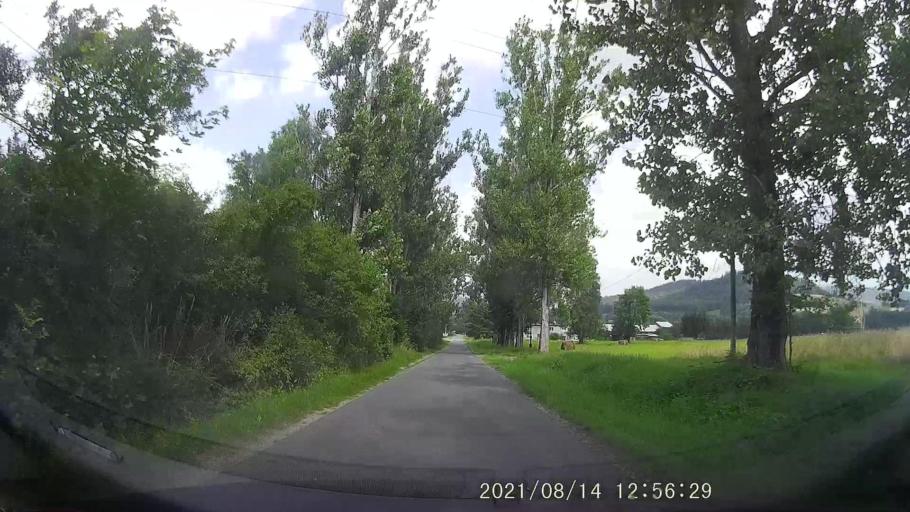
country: PL
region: Lower Silesian Voivodeship
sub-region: Powiat klodzki
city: Ladek-Zdroj
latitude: 50.3374
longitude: 16.8327
